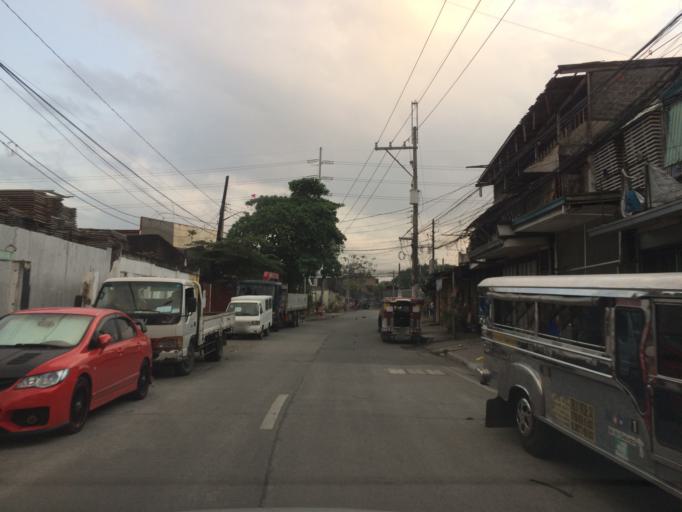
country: PH
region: Calabarzon
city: Bagong Pagasa
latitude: 14.6780
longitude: 121.0257
